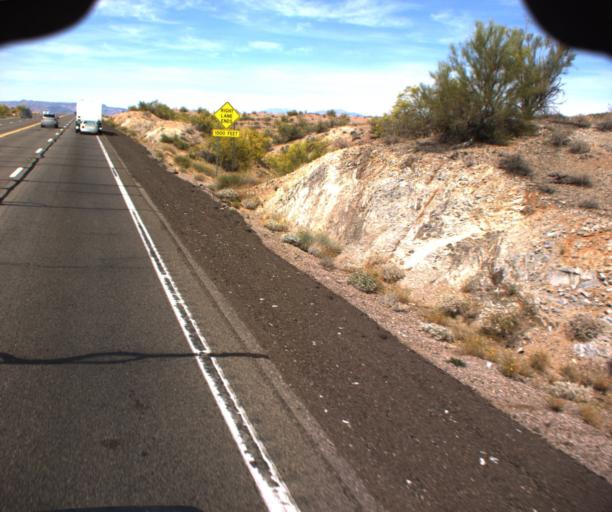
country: US
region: Arizona
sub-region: Mohave County
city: Desert Hills
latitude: 34.6447
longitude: -114.3225
